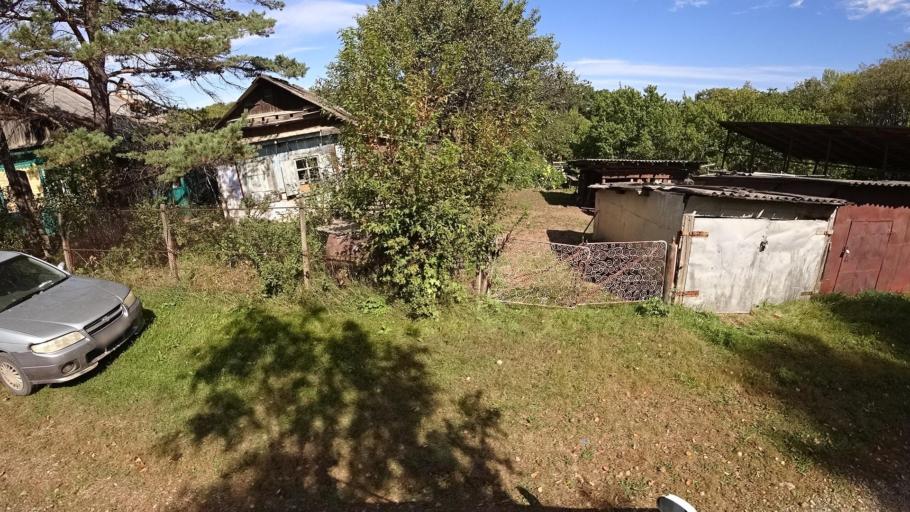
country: RU
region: Primorskiy
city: Kirovskiy
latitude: 44.7607
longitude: 133.6189
